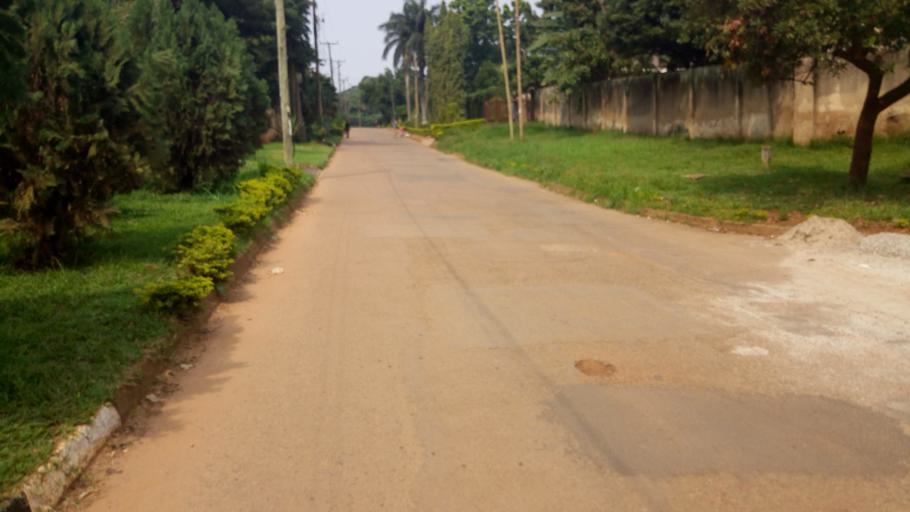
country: UG
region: Central Region
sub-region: Kampala District
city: Kampala
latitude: 0.3175
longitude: 32.6182
